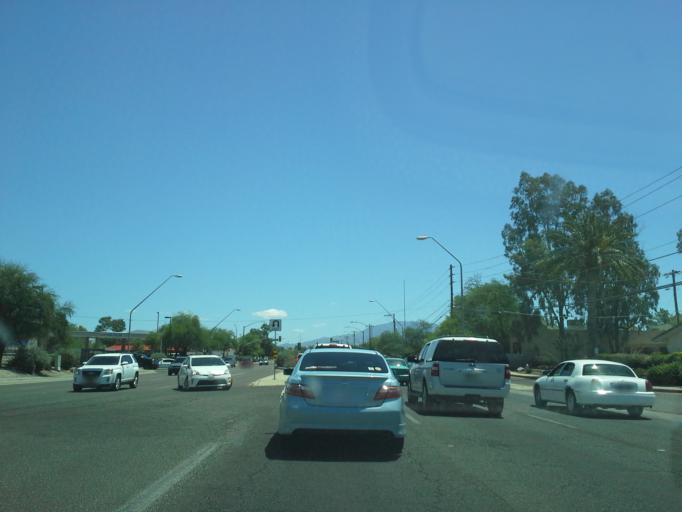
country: US
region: Arizona
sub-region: Pima County
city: Tucson
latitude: 32.2506
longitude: -110.8598
